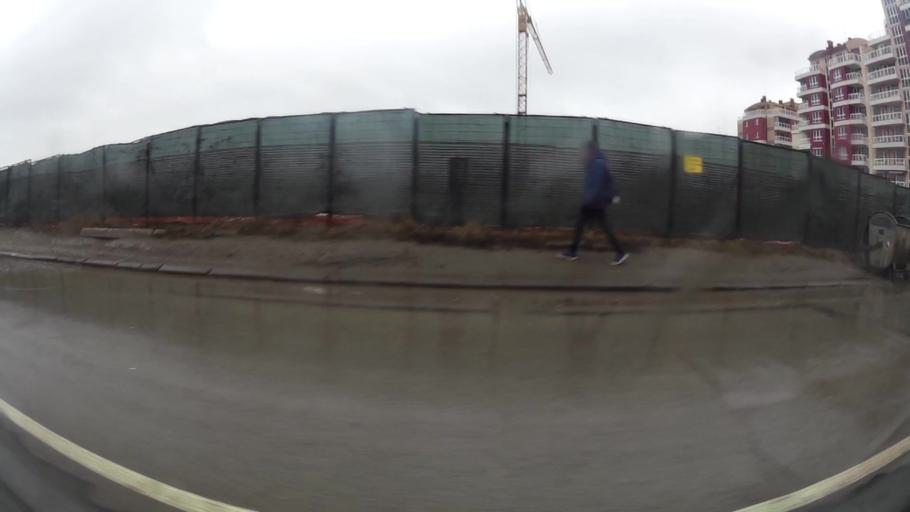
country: BG
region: Sofia-Capital
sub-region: Stolichna Obshtina
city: Sofia
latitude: 42.6308
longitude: 23.3812
